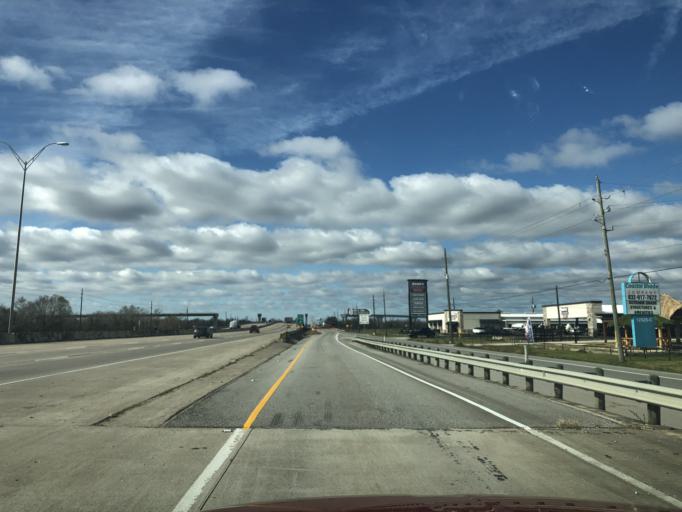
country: US
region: Texas
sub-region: Chambers County
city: Mont Belvieu
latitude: 29.8251
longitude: -94.8603
